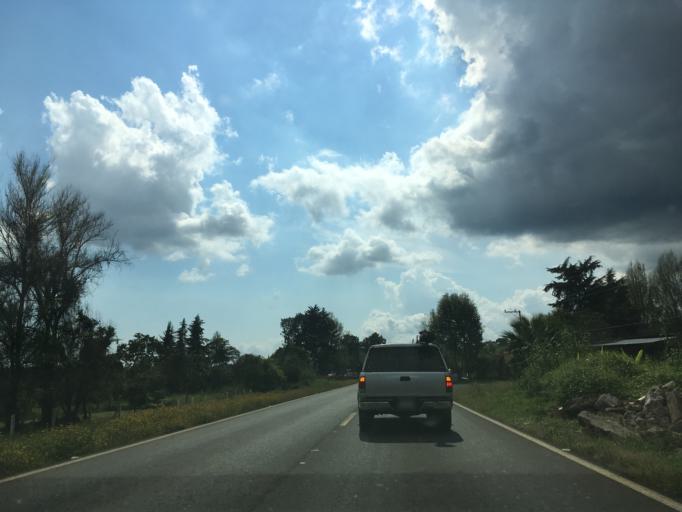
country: MX
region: Michoacan
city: Tingambato
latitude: 19.5017
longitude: -101.8673
